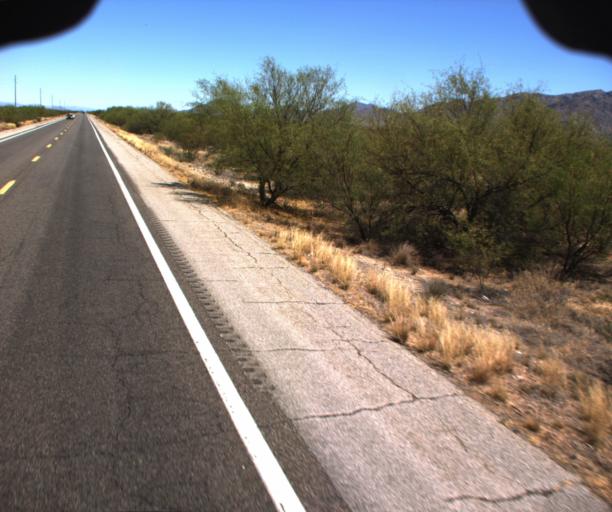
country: US
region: Arizona
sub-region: La Paz County
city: Salome
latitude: 33.8725
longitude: -113.3867
